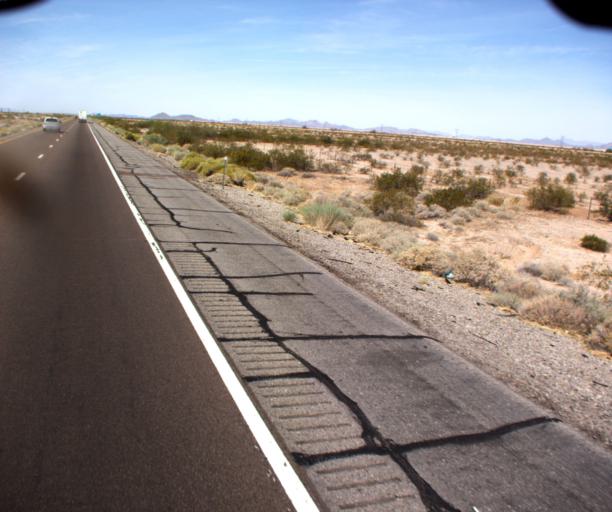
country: US
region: Arizona
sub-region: La Paz County
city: Salome
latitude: 33.5650
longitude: -113.3244
